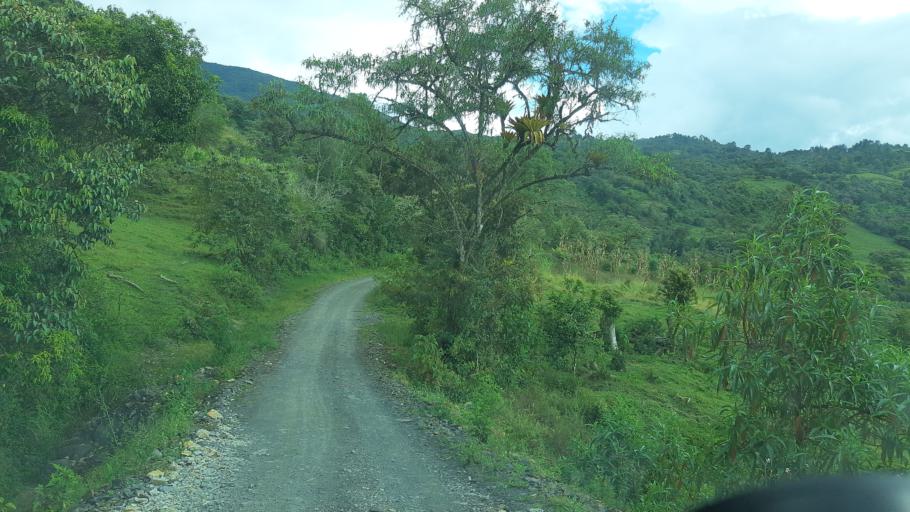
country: CO
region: Boyaca
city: Garagoa
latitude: 5.0265
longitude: -73.3283
